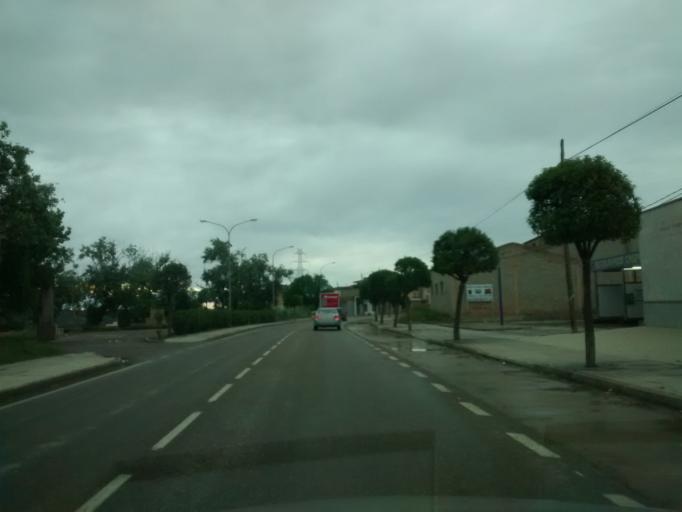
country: ES
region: Aragon
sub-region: Provincia de Zaragoza
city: Caspe
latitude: 41.2267
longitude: -0.0324
